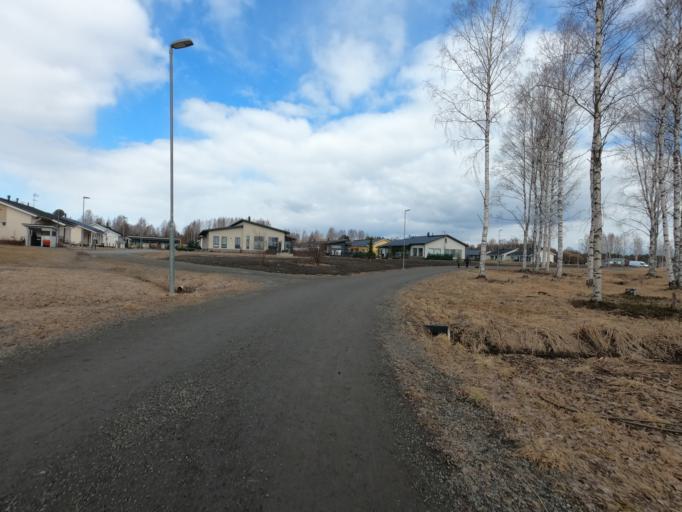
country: FI
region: North Karelia
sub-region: Joensuu
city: Joensuu
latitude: 62.6147
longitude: 29.8558
